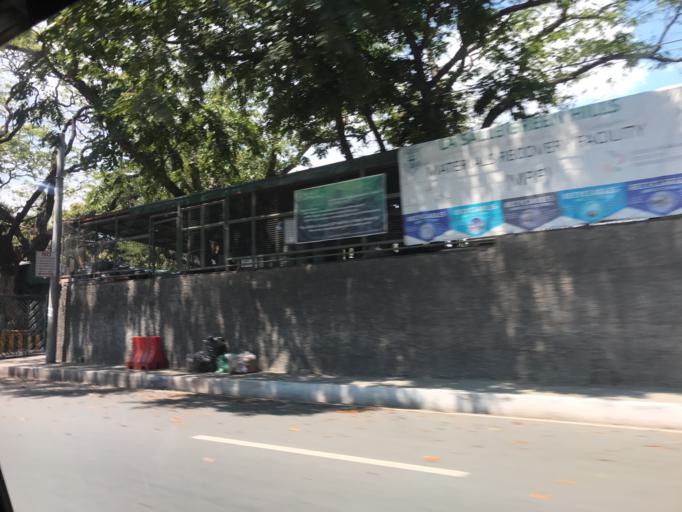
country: PH
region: Metro Manila
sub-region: Pasig
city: Pasig City
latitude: 14.5965
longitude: 121.0540
